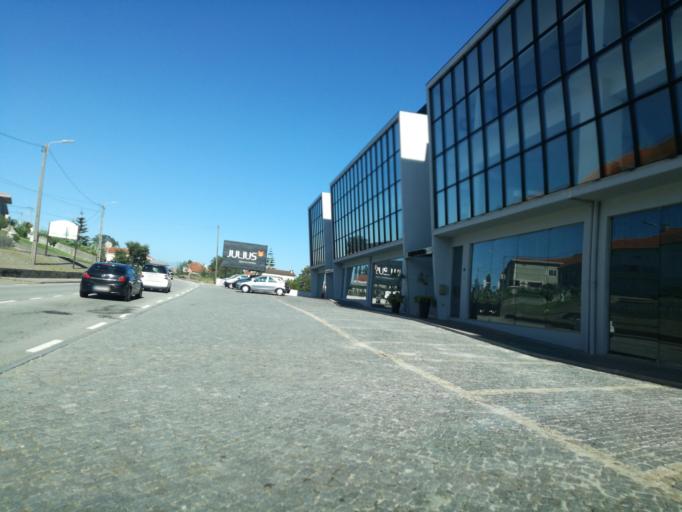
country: PT
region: Porto
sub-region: Pacos de Ferreira
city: Seroa
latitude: 41.2615
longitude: -8.4385
